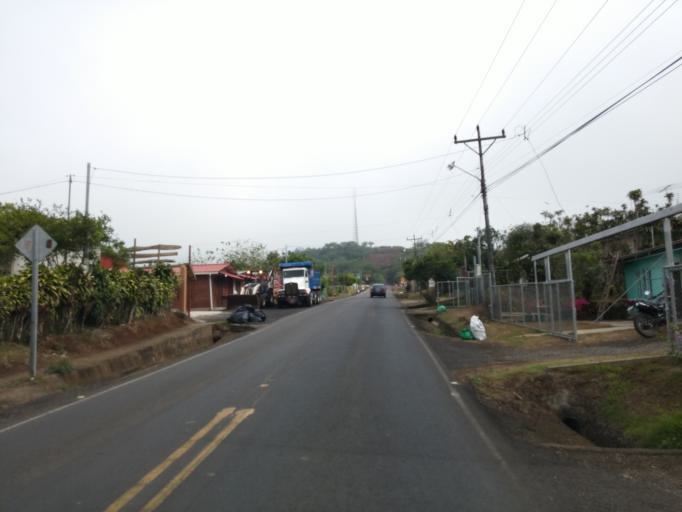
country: CR
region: Alajuela
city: San Ramon
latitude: 10.1342
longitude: -84.4747
